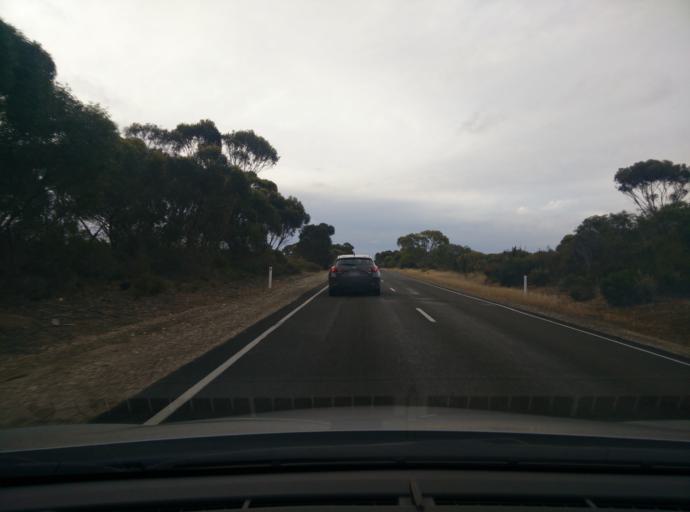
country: AU
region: South Australia
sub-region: Kangaroo Island
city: Kingscote
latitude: -35.7978
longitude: 137.6624
